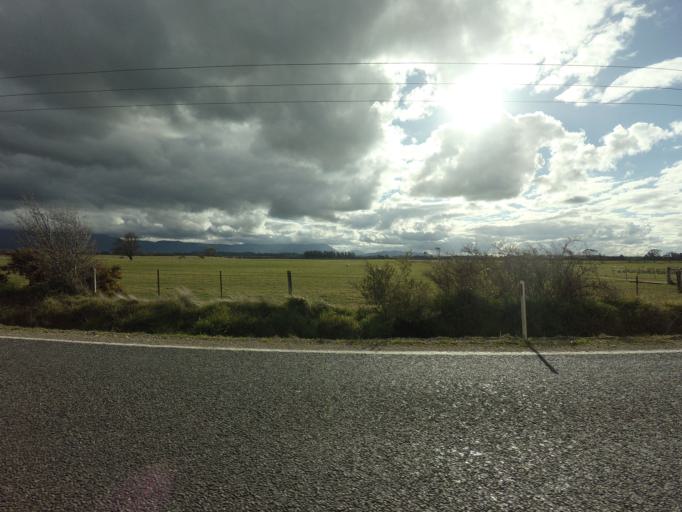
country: AU
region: Tasmania
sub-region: Northern Midlands
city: Longford
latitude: -41.7393
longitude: 147.0831
